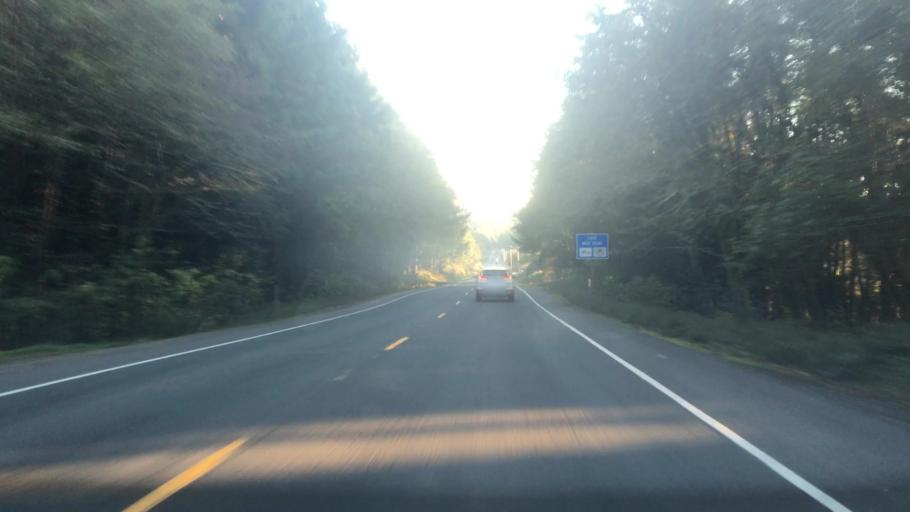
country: US
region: Oregon
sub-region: Clatsop County
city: Cannon Beach
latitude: 45.8770
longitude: -123.9578
